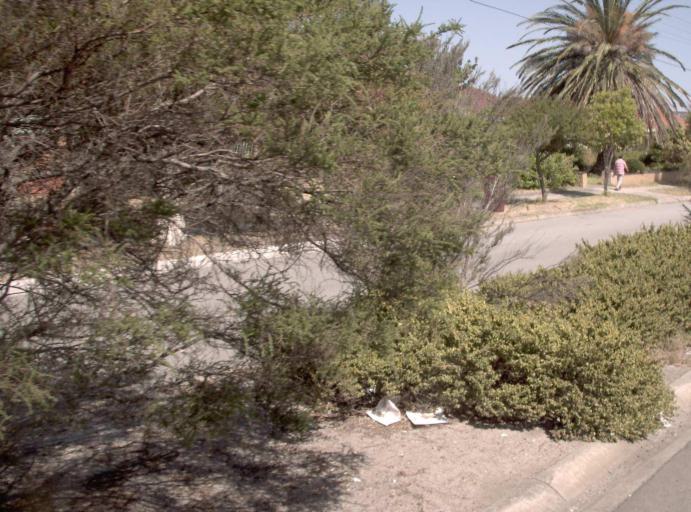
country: AU
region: Victoria
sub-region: Greater Dandenong
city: Springvale
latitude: -37.9530
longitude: 145.1381
